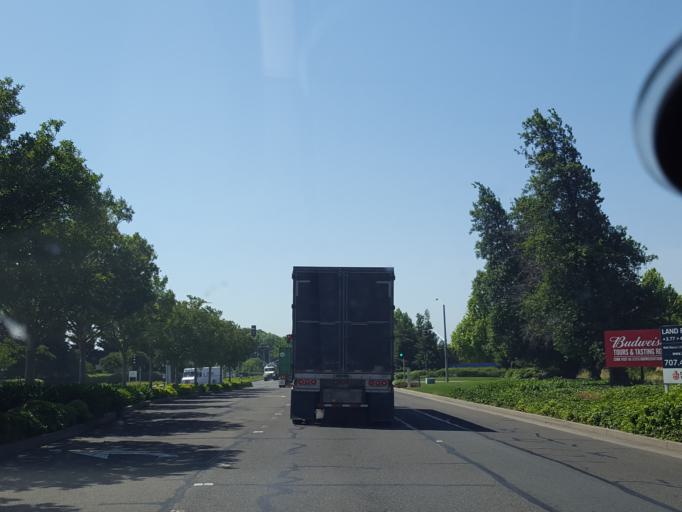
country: US
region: California
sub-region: Solano County
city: Suisun
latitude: 38.2388
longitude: -122.0842
